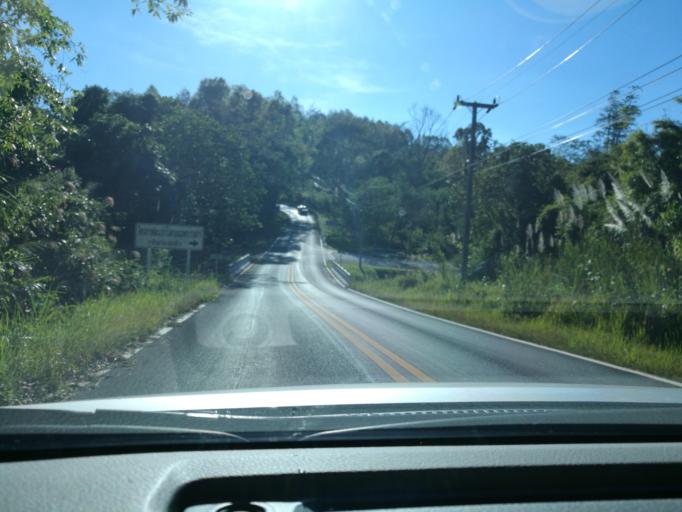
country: TH
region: Phitsanulok
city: Nakhon Thai
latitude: 16.9987
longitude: 101.0101
